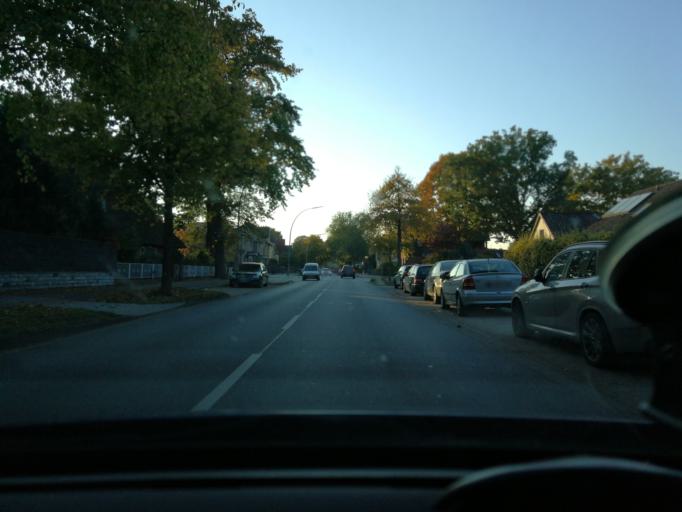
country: DE
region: Hamburg
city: Altona
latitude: 53.4777
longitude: 9.8930
